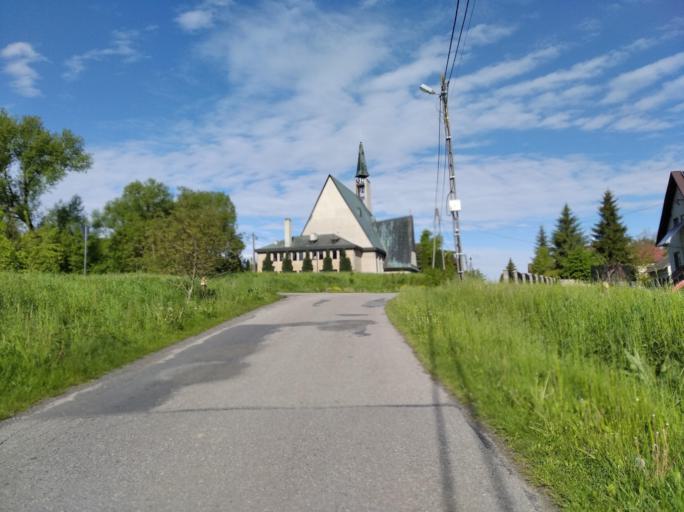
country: PL
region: Subcarpathian Voivodeship
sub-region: Powiat strzyzowski
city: Frysztak
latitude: 49.8476
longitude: 21.5299
